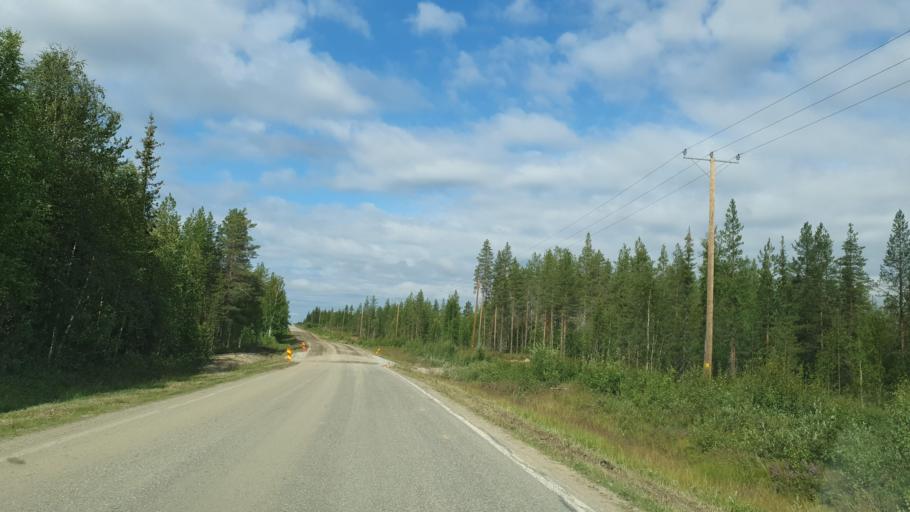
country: FI
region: Lapland
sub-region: Pohjois-Lappi
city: Sodankylae
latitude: 67.5356
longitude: 25.9703
